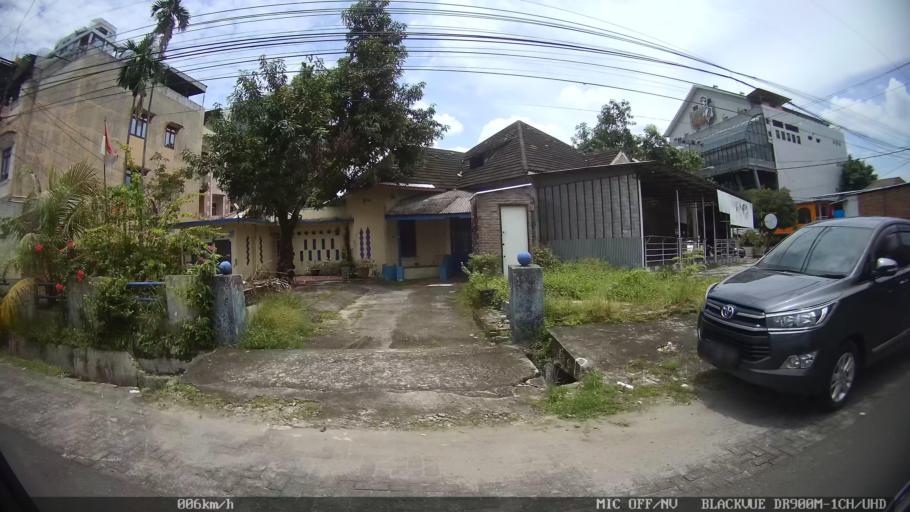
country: ID
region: North Sumatra
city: Medan
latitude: 3.5831
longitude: 98.6661
